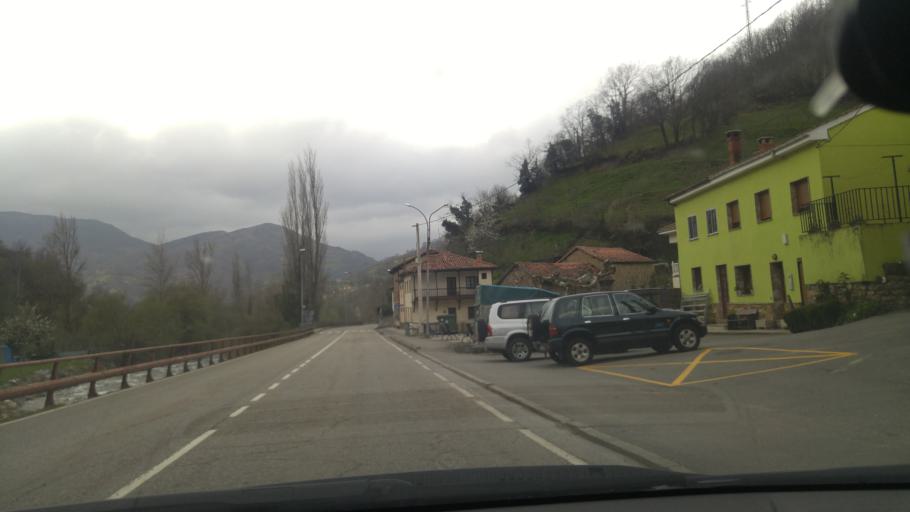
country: ES
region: Asturias
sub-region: Province of Asturias
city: Rio Aller
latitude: 43.1196
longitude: -5.5444
